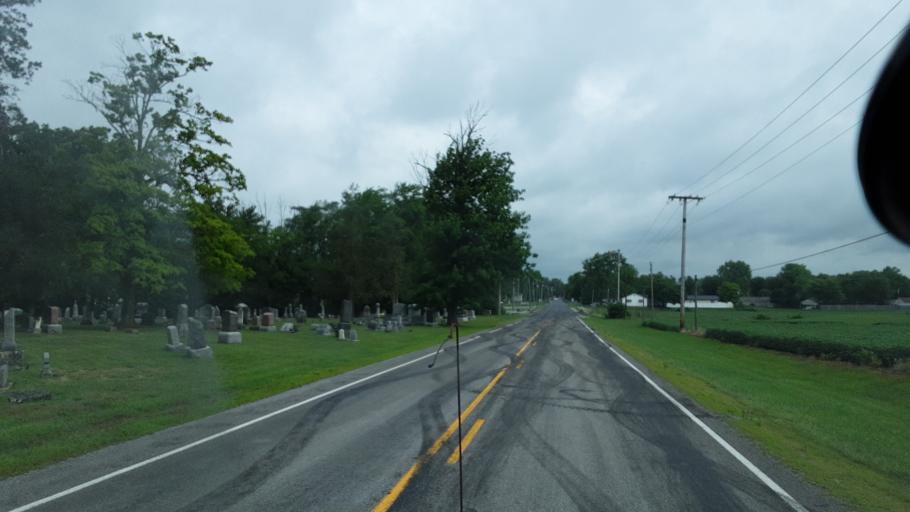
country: US
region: Indiana
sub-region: Allen County
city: Monroeville
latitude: 40.9654
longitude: -84.8628
